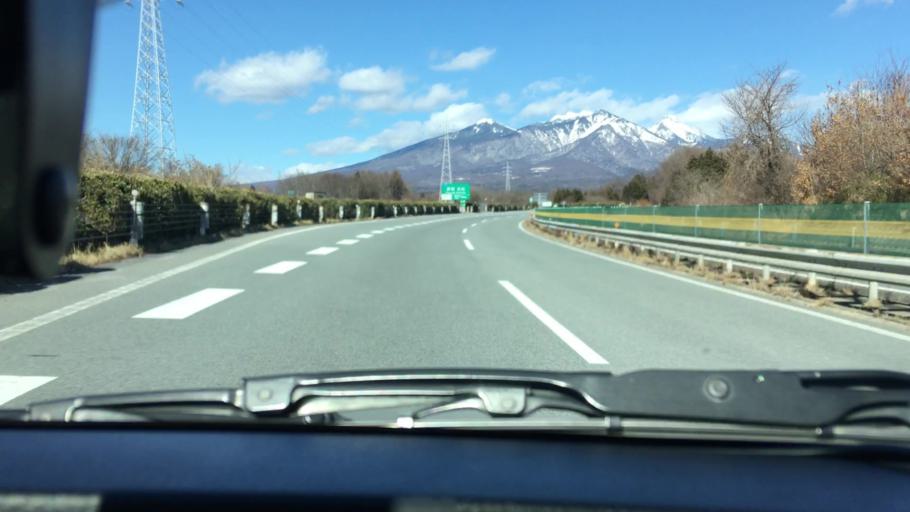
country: JP
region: Yamanashi
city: Nirasaki
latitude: 35.8258
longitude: 138.3929
